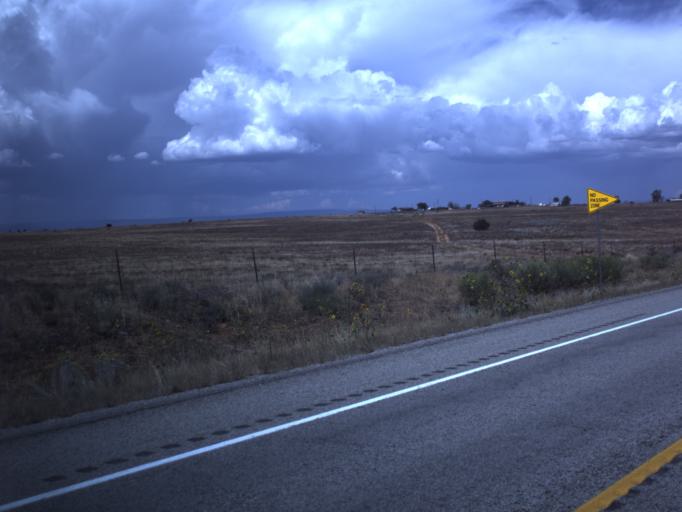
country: US
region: Utah
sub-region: San Juan County
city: Blanding
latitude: 37.4496
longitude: -109.4671
